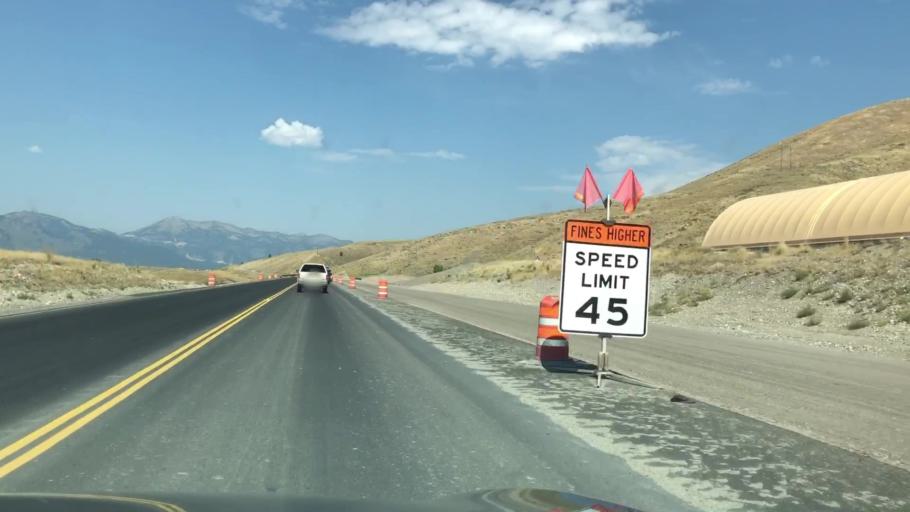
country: US
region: Wyoming
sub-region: Teton County
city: South Park
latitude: 43.4016
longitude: -110.7544
